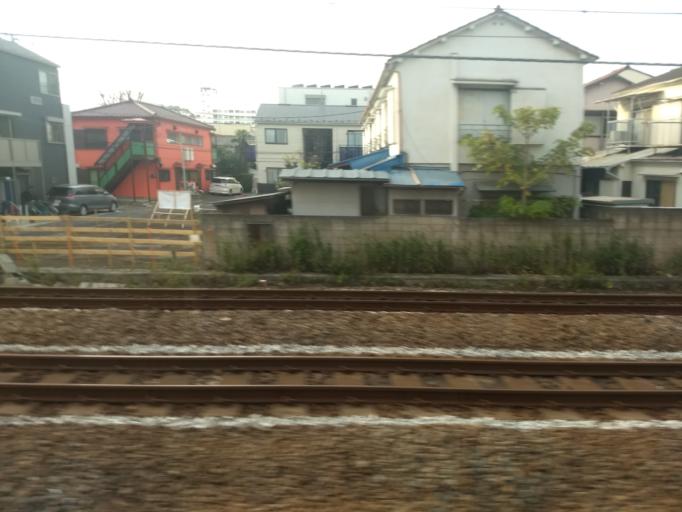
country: JP
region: Kanagawa
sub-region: Kawasaki-shi
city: Kawasaki
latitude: 35.5973
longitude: 139.7335
